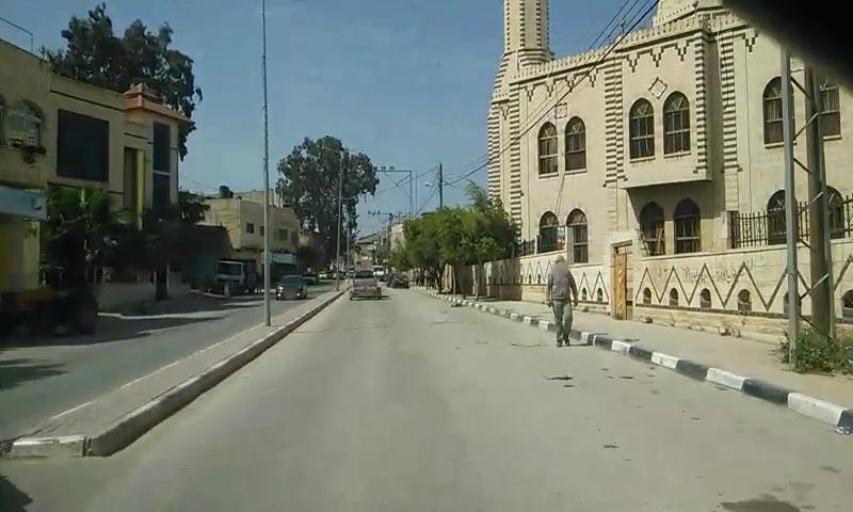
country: PS
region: West Bank
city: Qabatiyah
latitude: 32.4097
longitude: 35.2853
